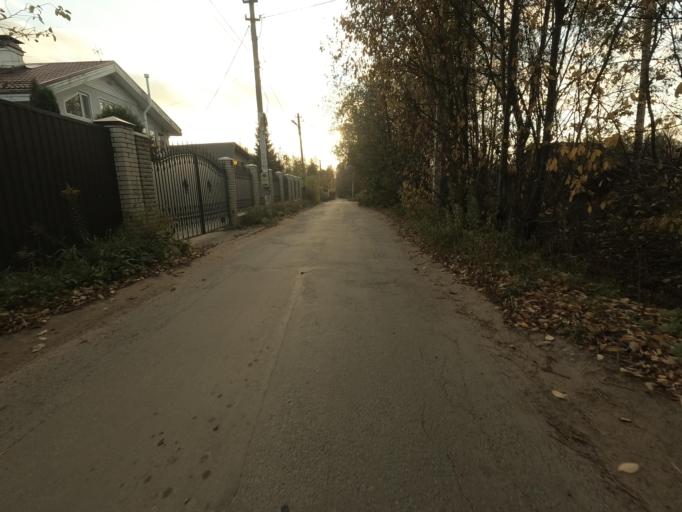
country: RU
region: St.-Petersburg
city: Beloostrov
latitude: 60.1845
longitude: 30.0560
